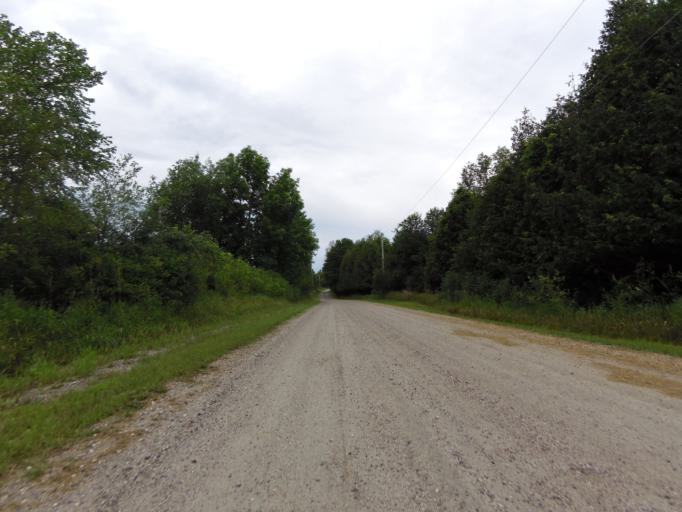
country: CA
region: Ontario
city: Perth
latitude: 45.0520
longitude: -76.3939
